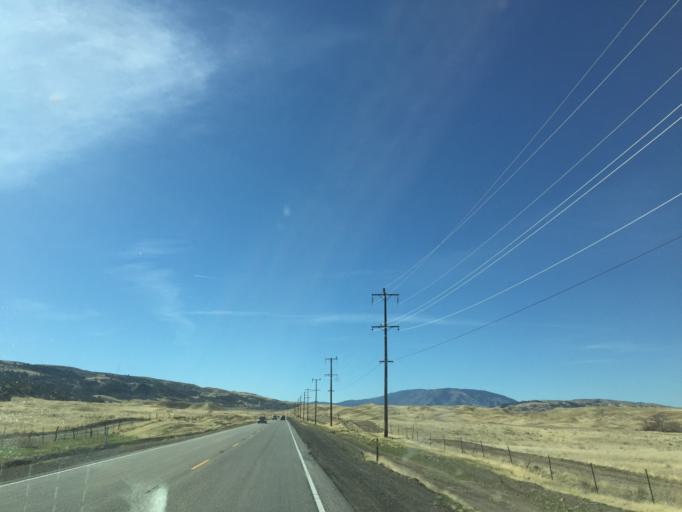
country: US
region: California
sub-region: Kern County
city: Lebec
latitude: 34.7734
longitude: -118.6856
